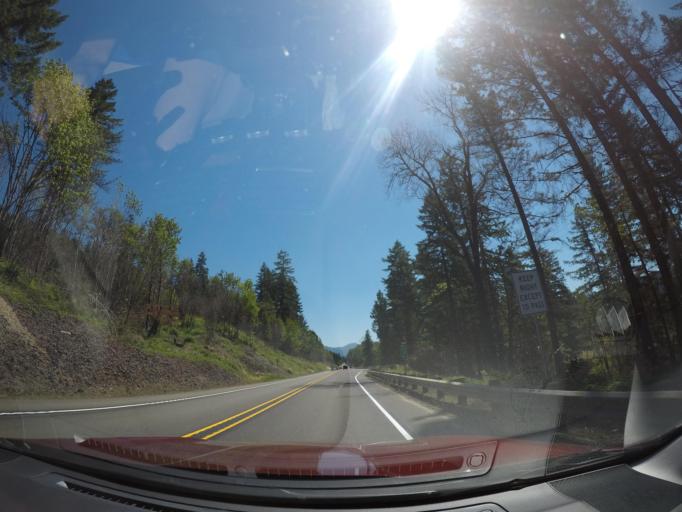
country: US
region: Oregon
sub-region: Linn County
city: Mill City
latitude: 44.7563
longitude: -122.4601
